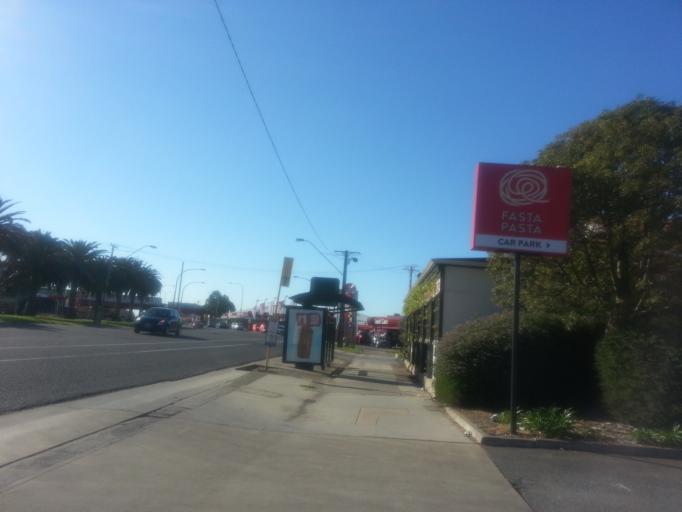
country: AU
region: South Australia
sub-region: Port Adelaide Enfield
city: Alberton
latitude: -34.8510
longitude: 138.5096
